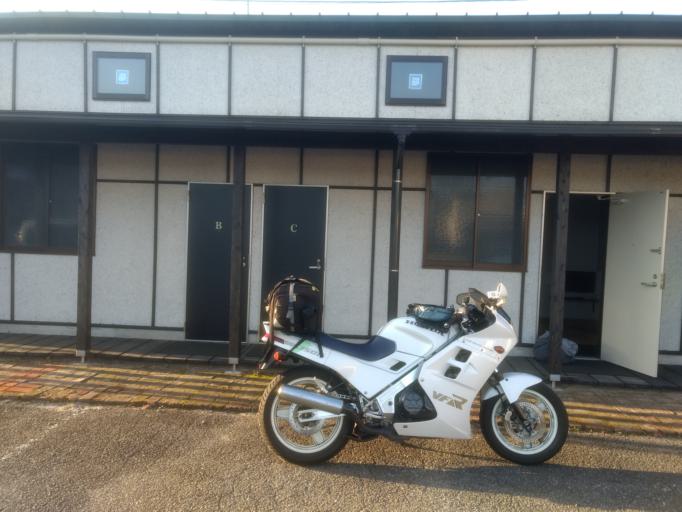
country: JP
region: Yamaguchi
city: Nagato
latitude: 34.3679
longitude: 131.1833
